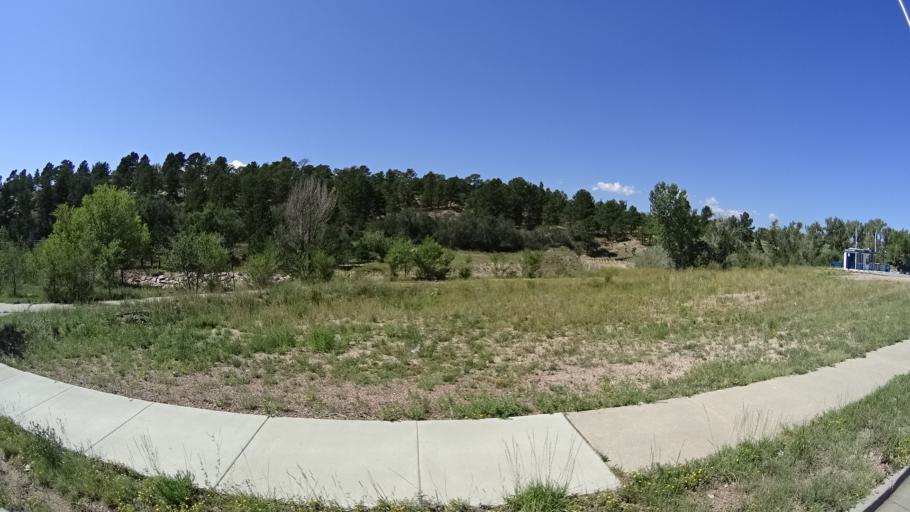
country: US
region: Colorado
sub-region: El Paso County
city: Cimarron Hills
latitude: 38.8539
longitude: -104.7235
